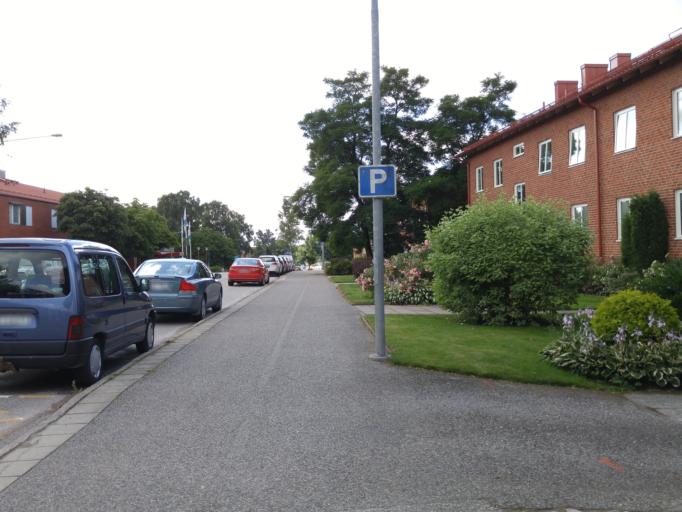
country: SE
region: Skane
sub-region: Hoors Kommun
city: Hoeoer
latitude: 55.9328
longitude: 13.5414
